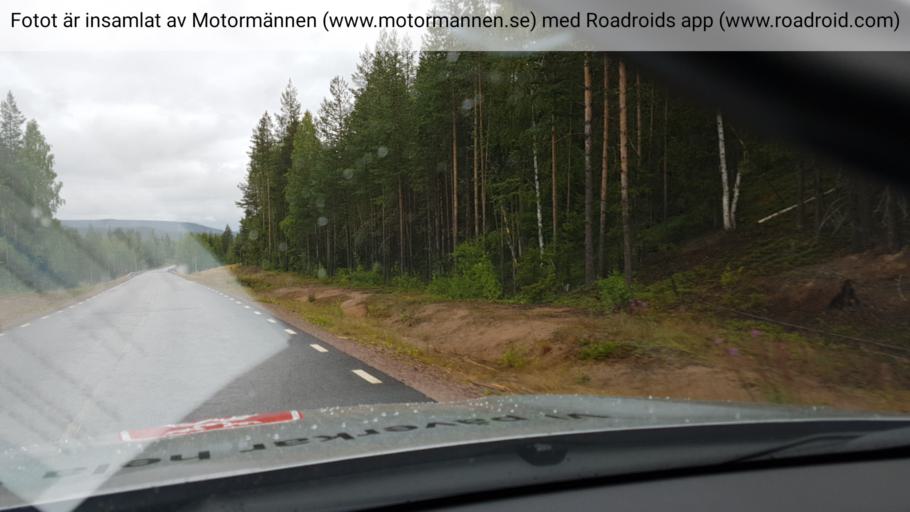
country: SE
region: Norrbotten
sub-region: Gallivare Kommun
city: Gaellivare
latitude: 66.6181
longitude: 20.4311
